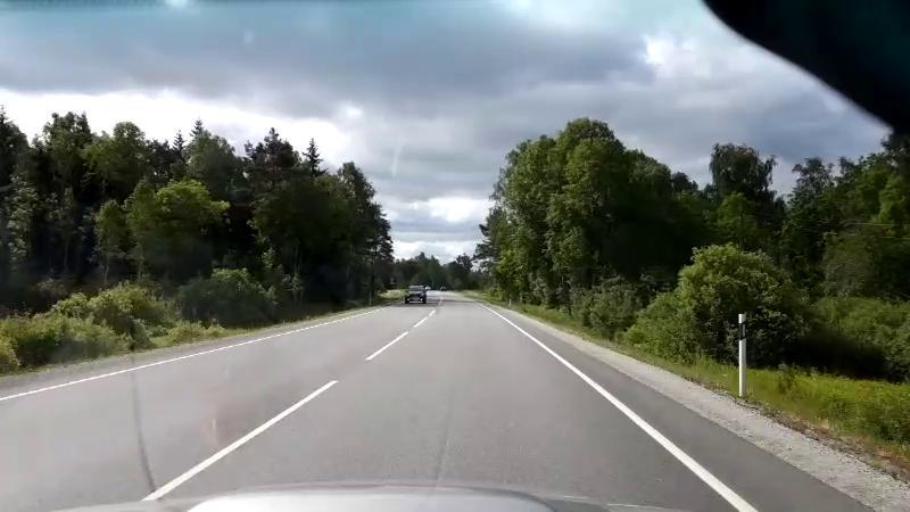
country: EE
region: Raplamaa
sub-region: Maerjamaa vald
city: Marjamaa
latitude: 58.9666
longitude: 24.4769
